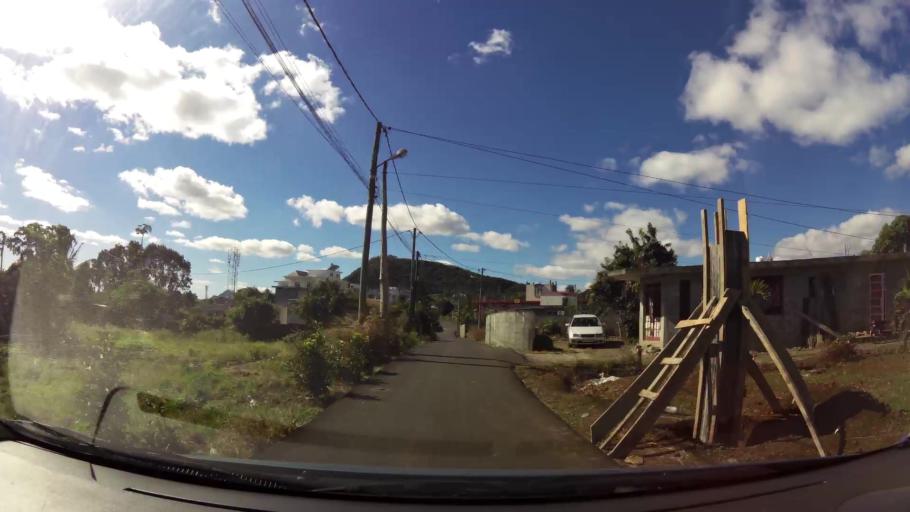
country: MU
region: Plaines Wilhems
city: Vacoas
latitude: -20.2837
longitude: 57.4768
